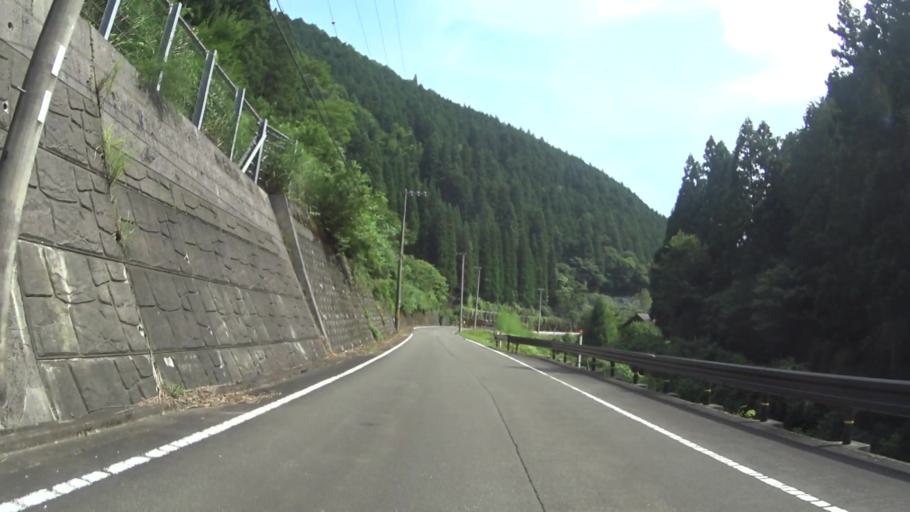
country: JP
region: Fukui
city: Obama
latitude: 35.3244
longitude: 135.6439
